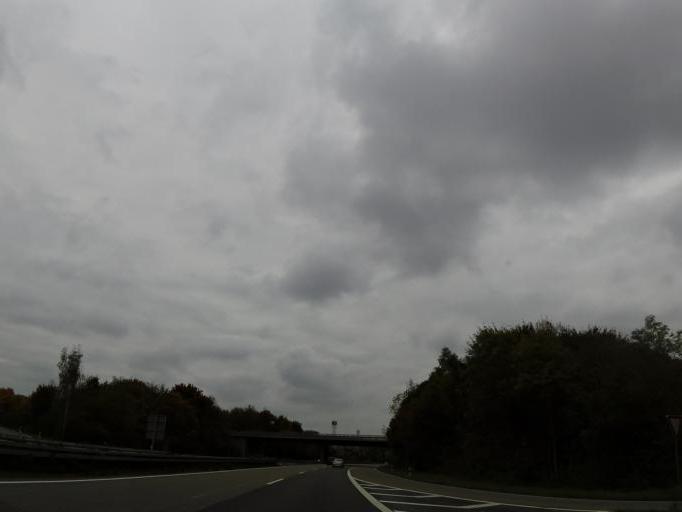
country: FR
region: Lorraine
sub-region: Departement de la Moselle
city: Spicheren
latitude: 49.2099
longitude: 6.9695
